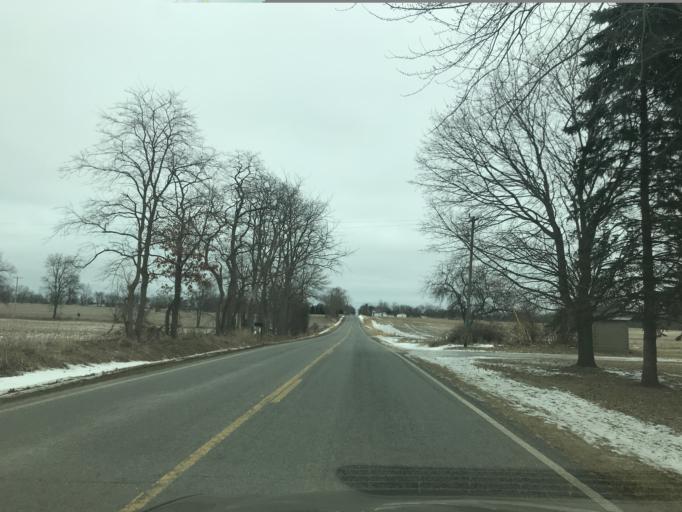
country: US
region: Michigan
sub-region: Jackson County
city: Brooklyn
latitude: 42.0734
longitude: -84.3469
